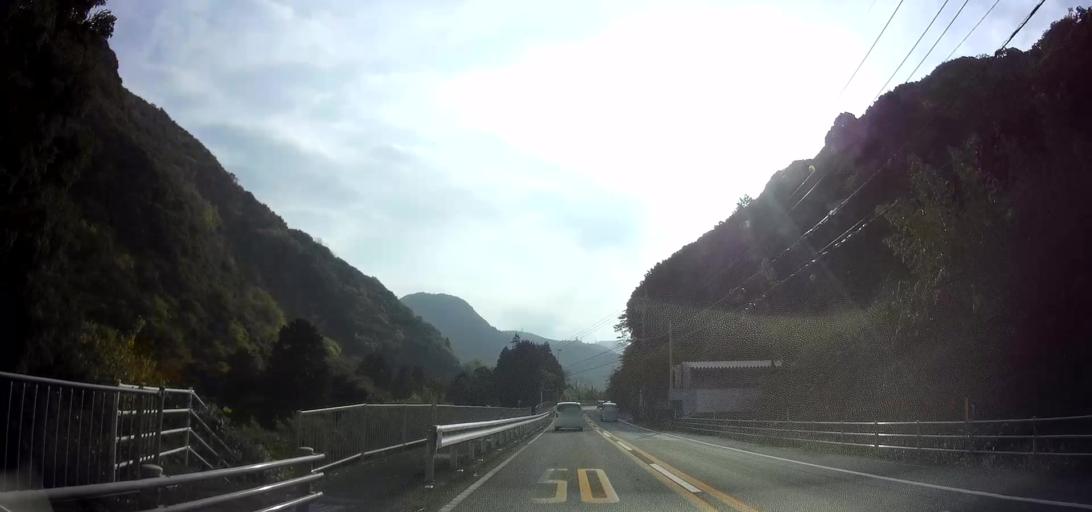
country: JP
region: Nagasaki
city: Shimabara
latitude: 32.7765
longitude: 130.2117
